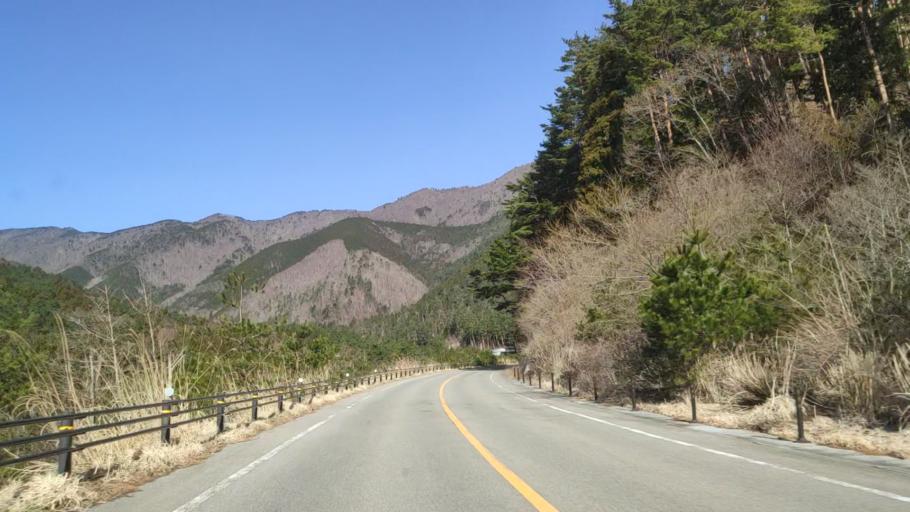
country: JP
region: Yamanashi
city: Fujikawaguchiko
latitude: 35.5257
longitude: 138.7203
